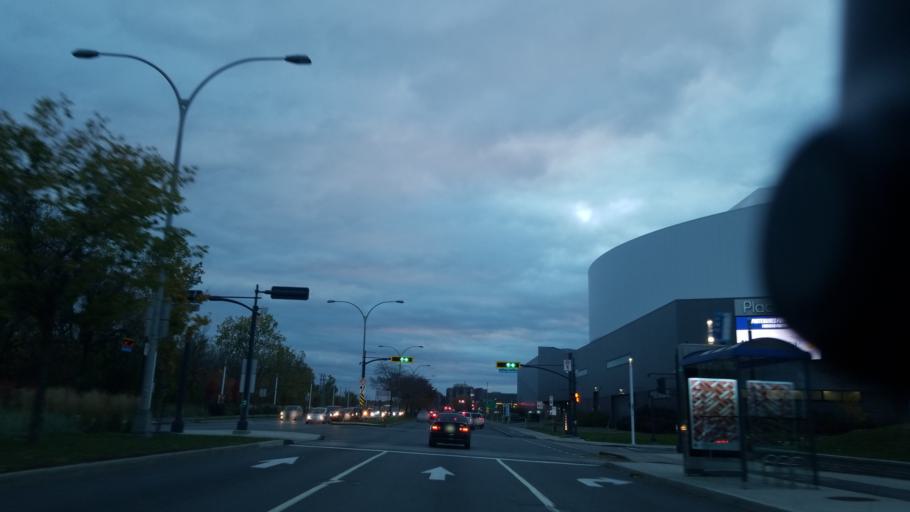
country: CA
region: Quebec
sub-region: Laval
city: Laval
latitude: 45.5562
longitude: -73.7194
